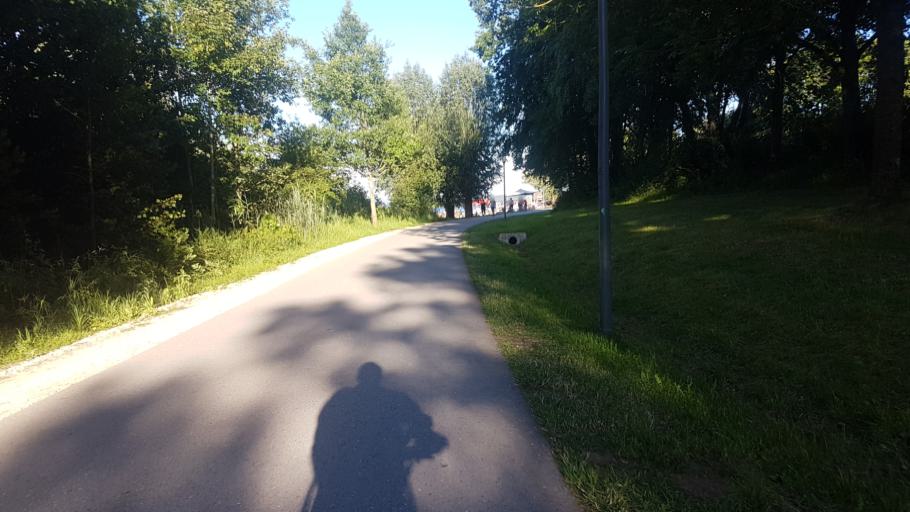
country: DE
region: Bavaria
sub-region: Regierungsbezirk Mittelfranken
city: Absberg
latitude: 49.1392
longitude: 10.8753
